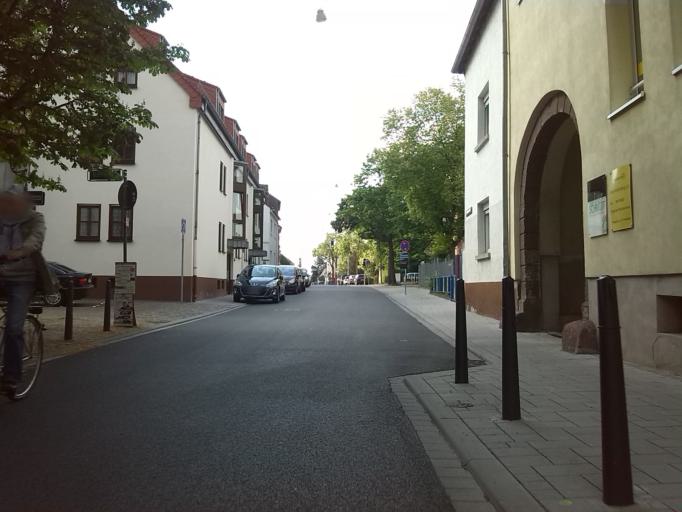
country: DE
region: Baden-Wuerttemberg
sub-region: Karlsruhe Region
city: Mannheim
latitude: 49.5136
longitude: 8.5165
